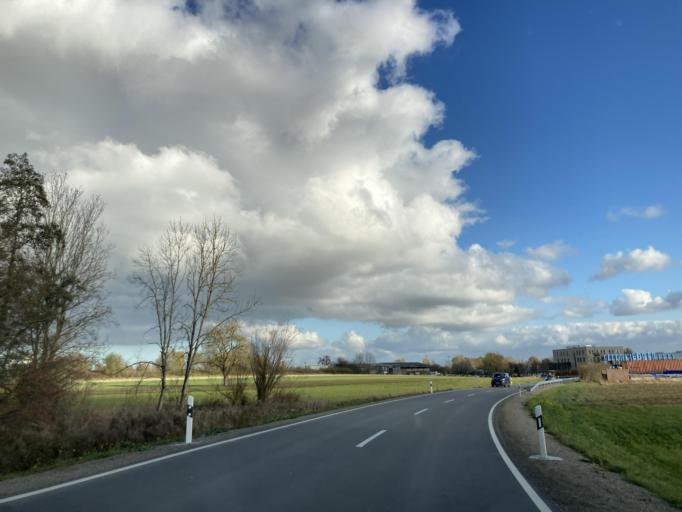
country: DE
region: Baden-Wuerttemberg
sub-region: Karlsruhe Region
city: Empfingen
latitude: 48.3996
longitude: 8.6954
